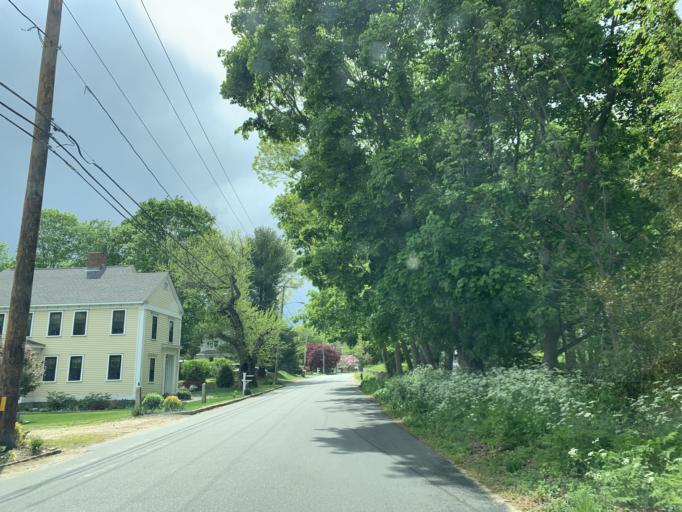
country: US
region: Rhode Island
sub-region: Providence County
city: Johnston
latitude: 41.8051
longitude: -71.4816
